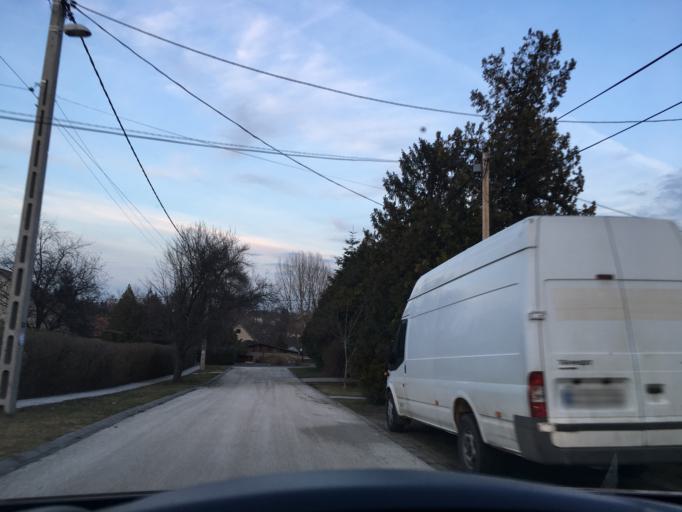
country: HU
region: Budapest
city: Budapest XVII. keruelet
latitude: 47.4742
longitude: 19.2861
